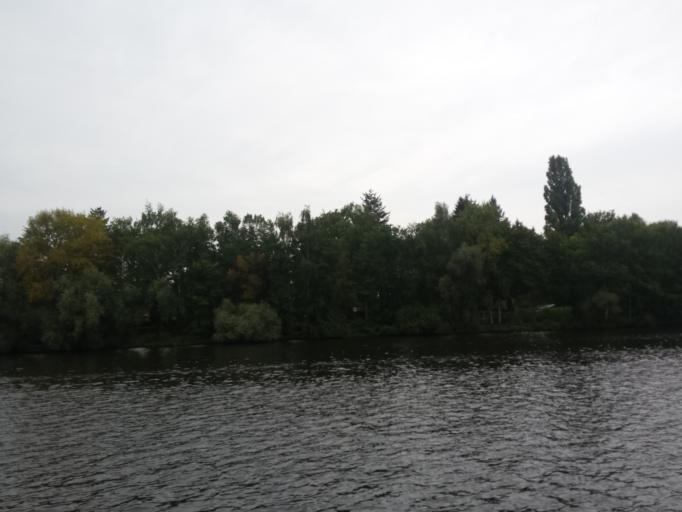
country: DE
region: Berlin
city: Kladow
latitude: 52.4269
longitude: 13.1080
